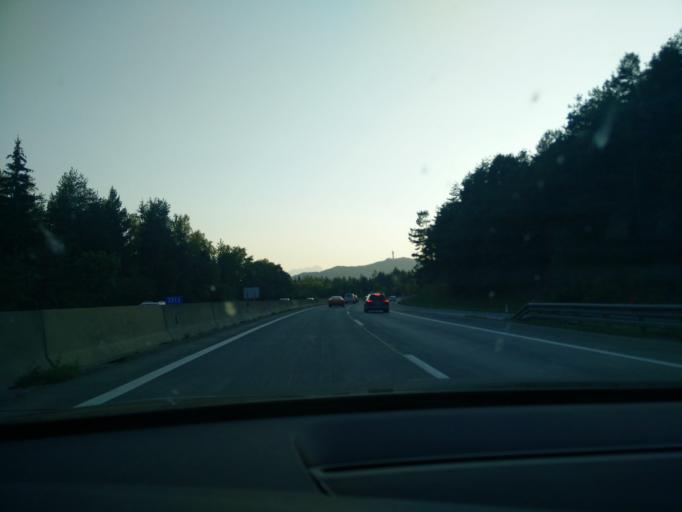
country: AT
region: Carinthia
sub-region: Politischer Bezirk Klagenfurt Land
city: Keutschach am See
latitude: 46.6281
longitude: 14.1980
